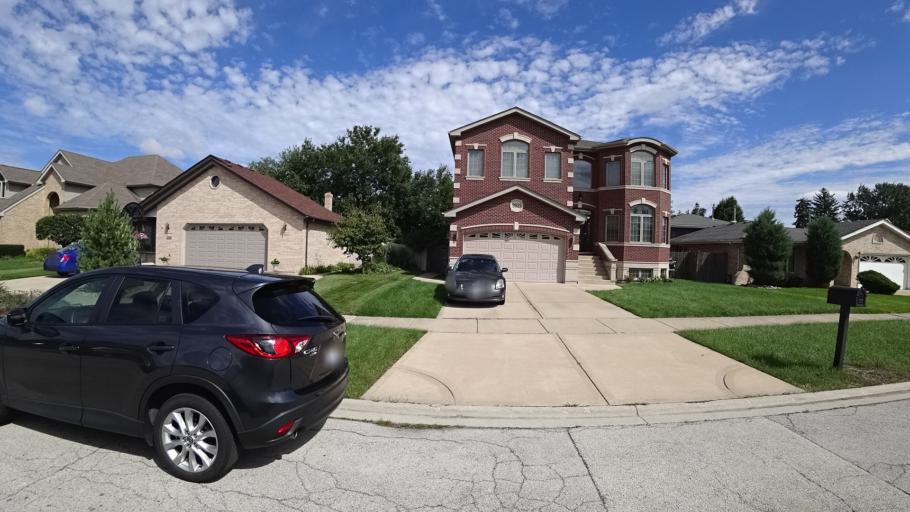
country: US
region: Illinois
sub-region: Cook County
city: Oak Lawn
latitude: 41.7134
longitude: -87.7711
